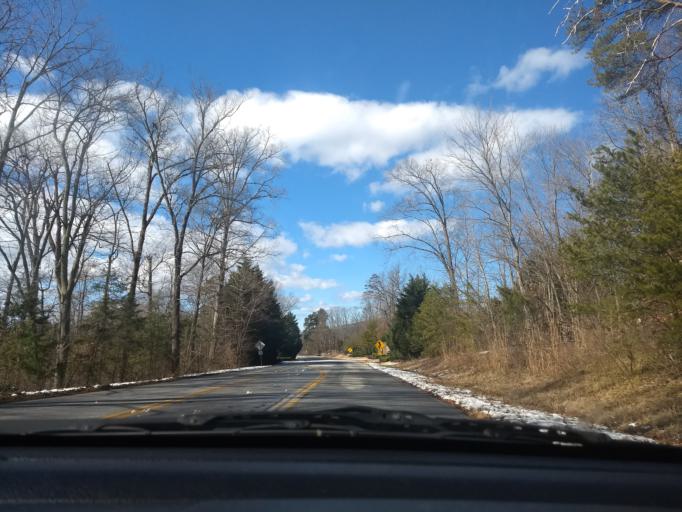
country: US
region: South Carolina
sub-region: Greenville County
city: Sans Souci
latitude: 34.9004
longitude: -82.3842
